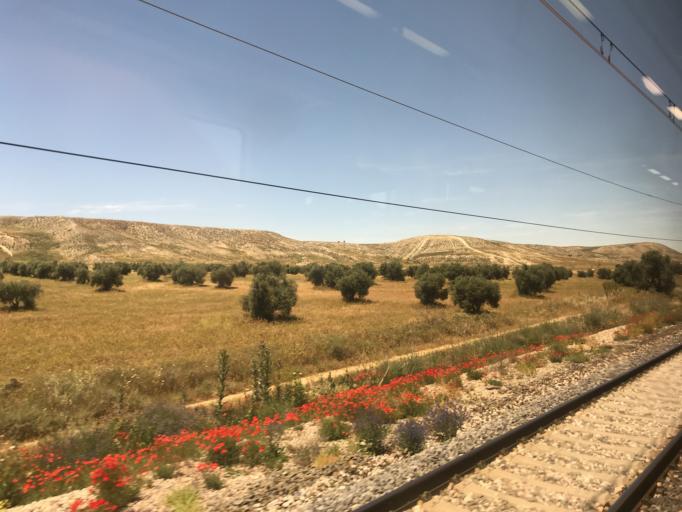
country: ES
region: Madrid
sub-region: Provincia de Madrid
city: Ciempozuelos
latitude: 40.1203
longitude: -3.6190
